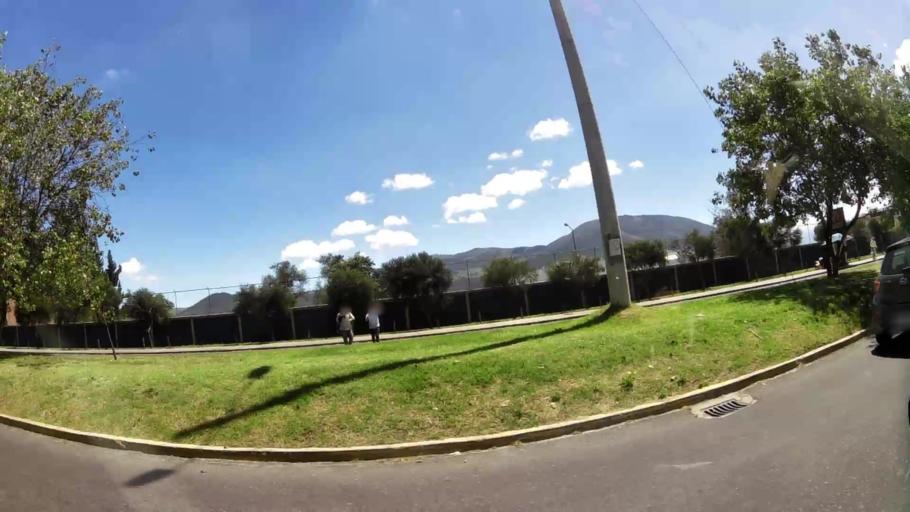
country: EC
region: Pichincha
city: Quito
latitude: -0.0912
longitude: -78.4764
